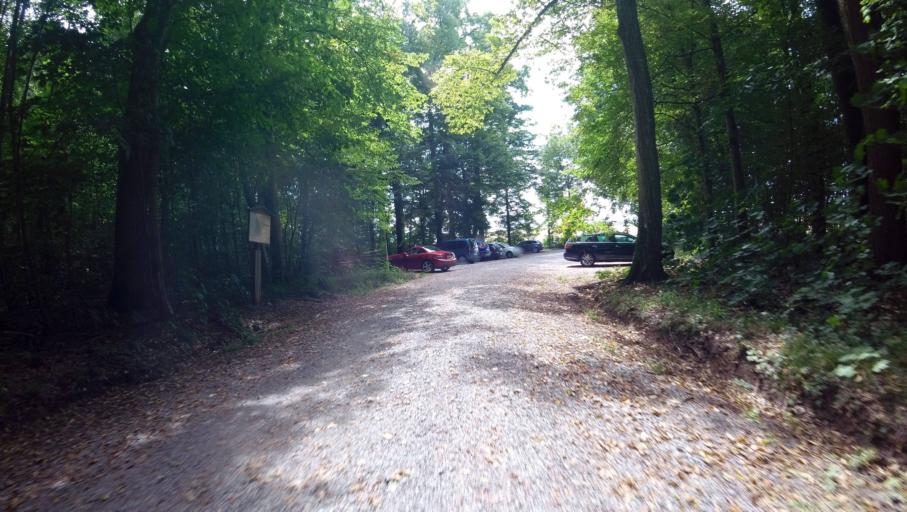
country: DE
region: Baden-Wuerttemberg
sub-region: Regierungsbezirk Stuttgart
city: Kirchberg an der Murr
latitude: 48.9669
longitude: 9.3573
